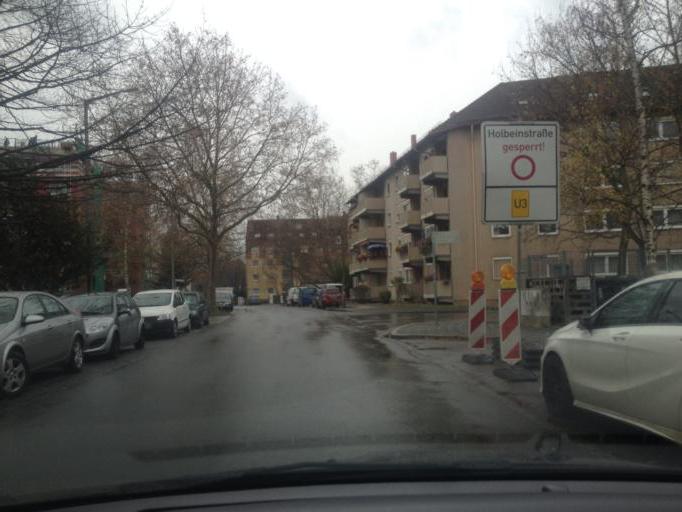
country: DE
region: Bavaria
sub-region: Regierungsbezirk Mittelfranken
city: Grossreuth bei Schweinau
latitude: 49.4341
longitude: 11.0527
